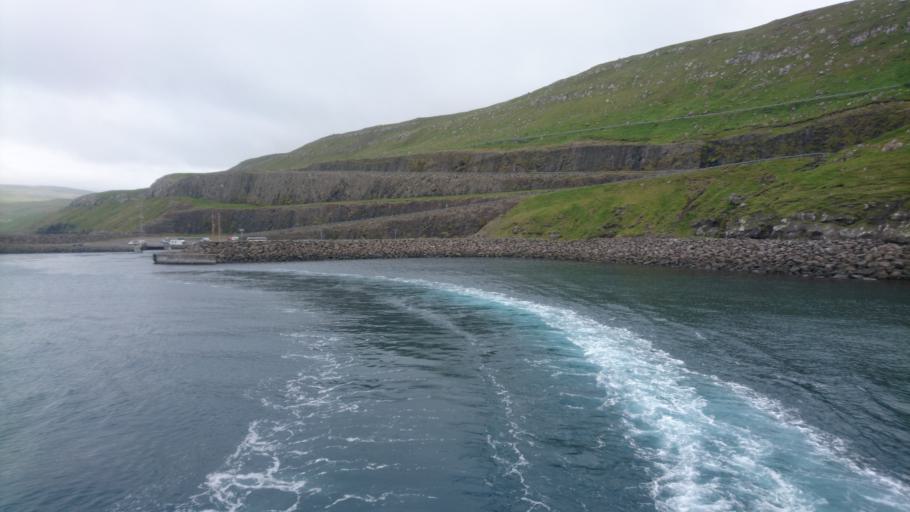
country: FO
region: Streymoy
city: Argir
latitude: 61.9594
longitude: -6.8161
